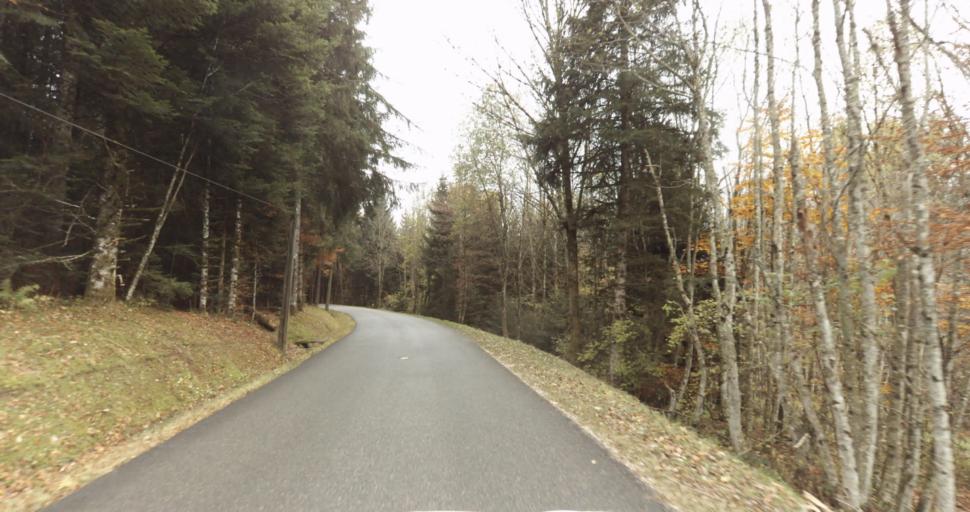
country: FR
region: Rhone-Alpes
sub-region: Departement de la Haute-Savoie
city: Gruffy
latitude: 45.7618
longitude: 6.1283
